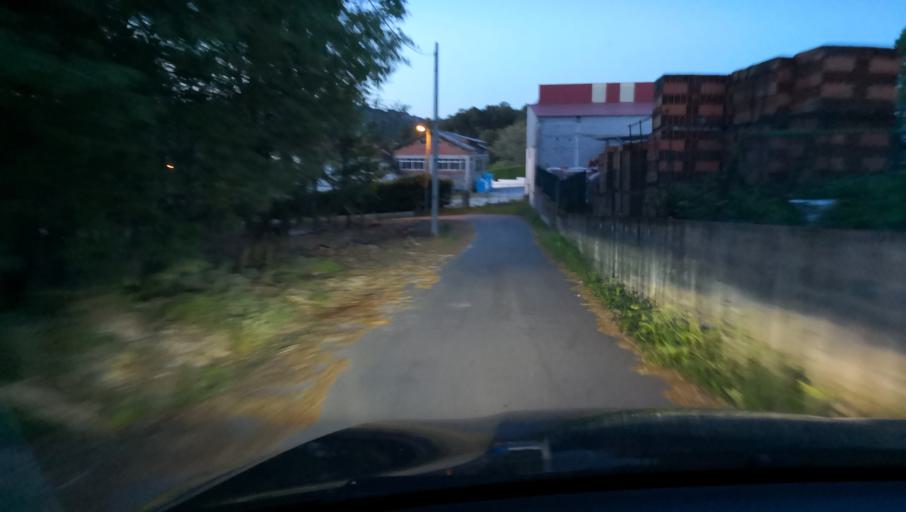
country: PT
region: Vila Real
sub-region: Vila Real
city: Vila Real
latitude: 41.3228
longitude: -7.6850
